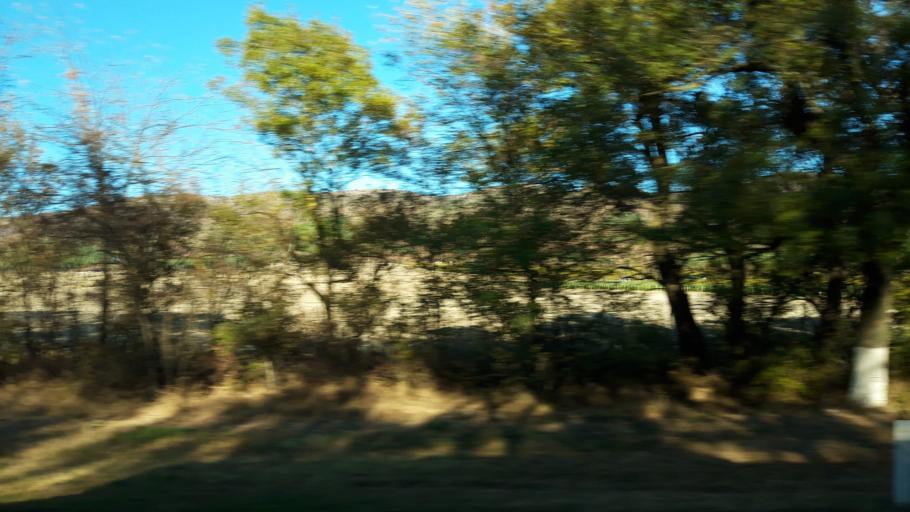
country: RU
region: Krasnodarskiy
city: Kabardinka
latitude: 44.6279
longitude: 38.0056
